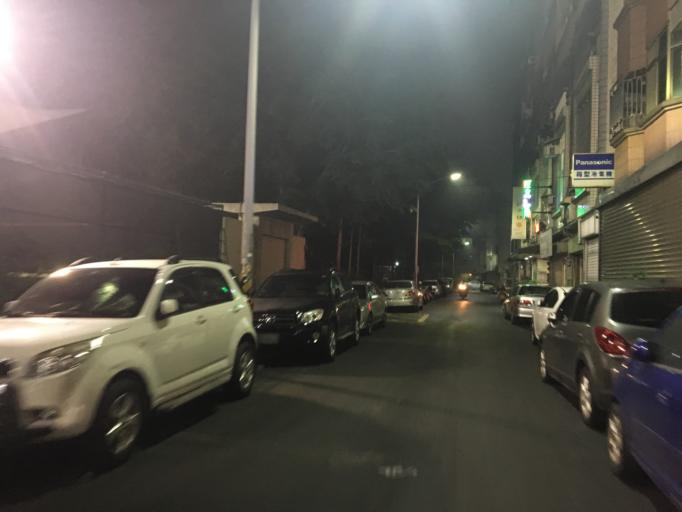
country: TW
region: Taiwan
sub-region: Hsinchu
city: Hsinchu
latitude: 24.8108
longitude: 120.9804
